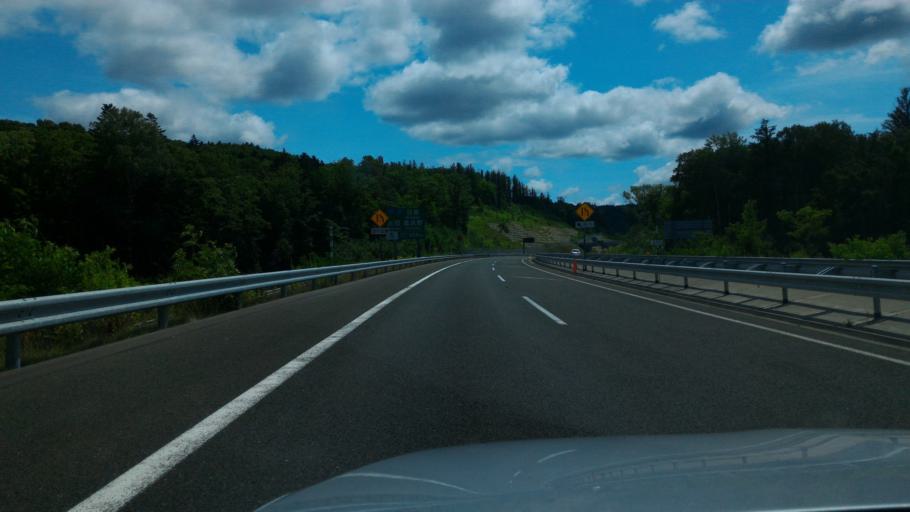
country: JP
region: Hokkaido
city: Shimo-furano
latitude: 42.9878
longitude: 142.4117
